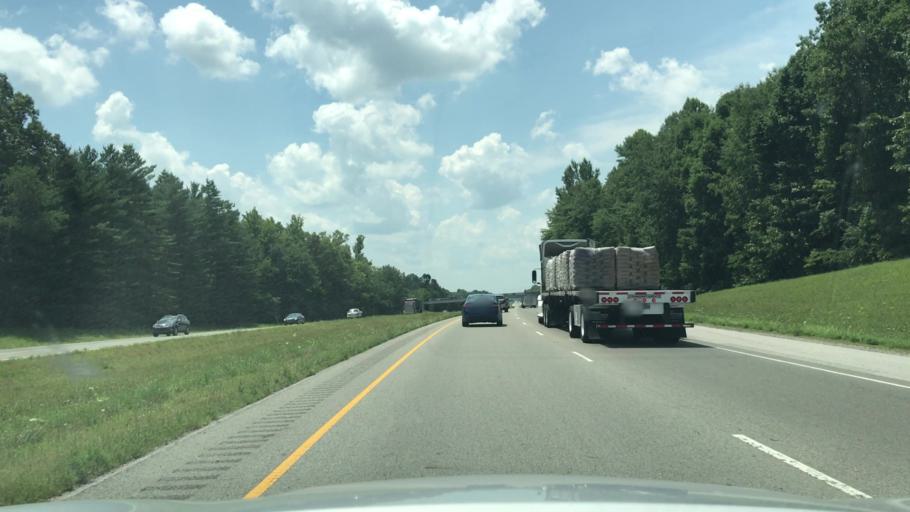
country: US
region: Tennessee
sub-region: Putnam County
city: Algood
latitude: 36.1706
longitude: -85.4618
